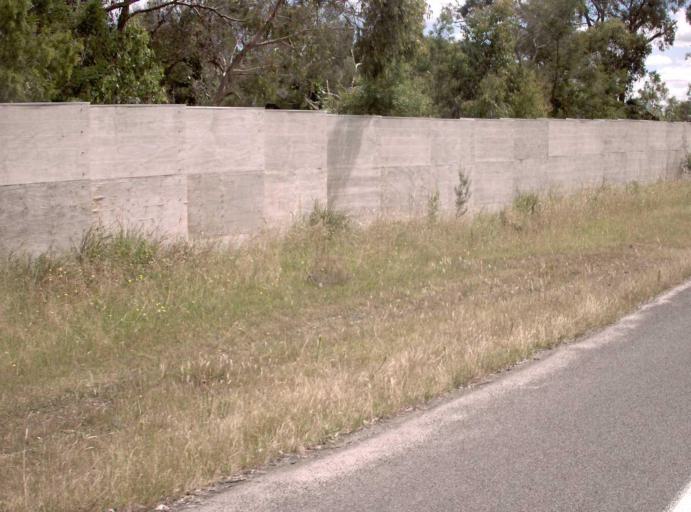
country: AU
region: Victoria
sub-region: Cardinia
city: Koo-Wee-Rup
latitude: -38.3804
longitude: 145.5544
